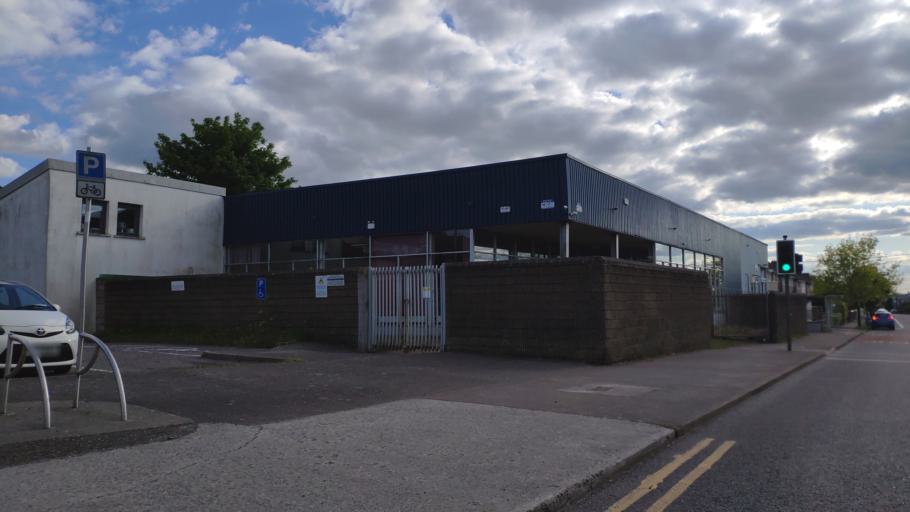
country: IE
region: Munster
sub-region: County Cork
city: Cork
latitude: 51.9110
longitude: -8.4439
